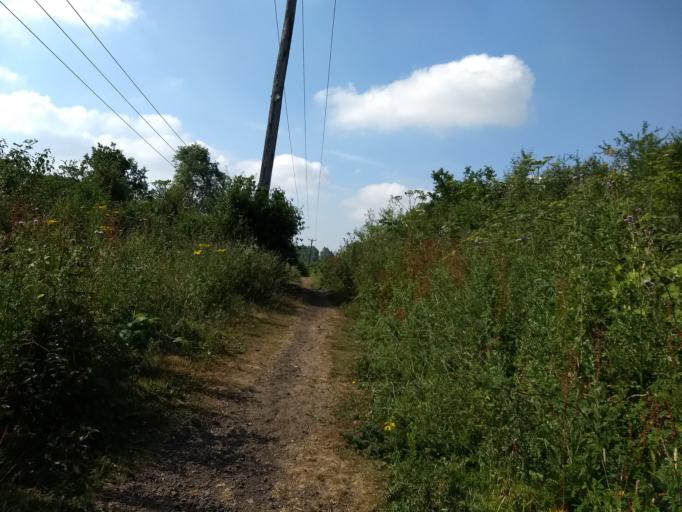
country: GB
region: England
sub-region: Isle of Wight
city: Ryde
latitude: 50.7195
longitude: -1.1603
